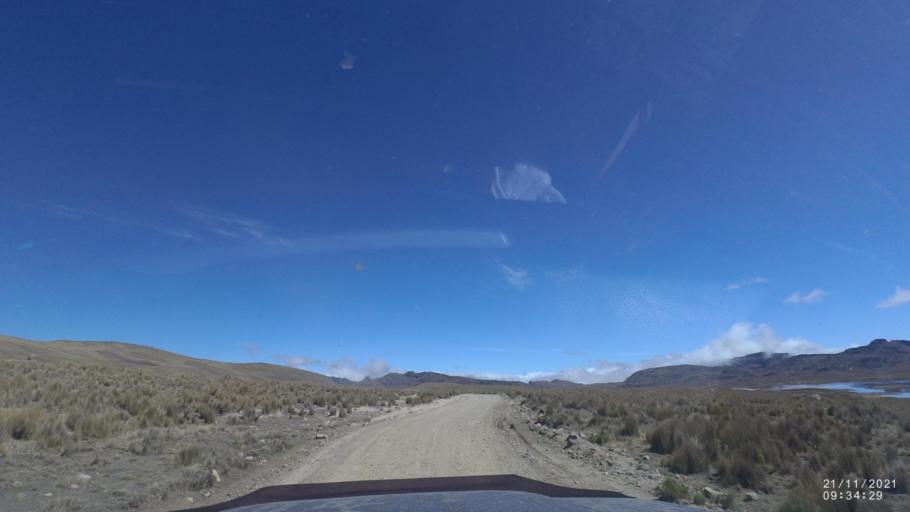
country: BO
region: Cochabamba
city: Cochabamba
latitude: -17.0566
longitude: -66.2598
